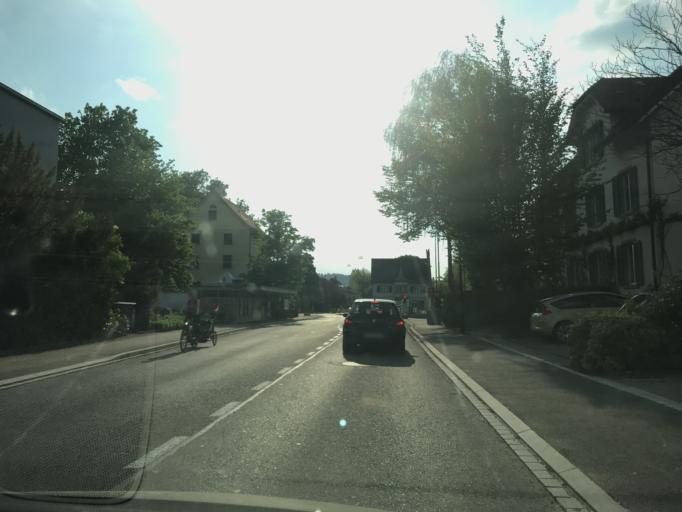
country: CH
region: Zurich
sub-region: Bezirk Winterthur
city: Stadt Winterthur (Kreis 1) / Heiligberg
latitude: 47.4903
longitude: 8.7267
